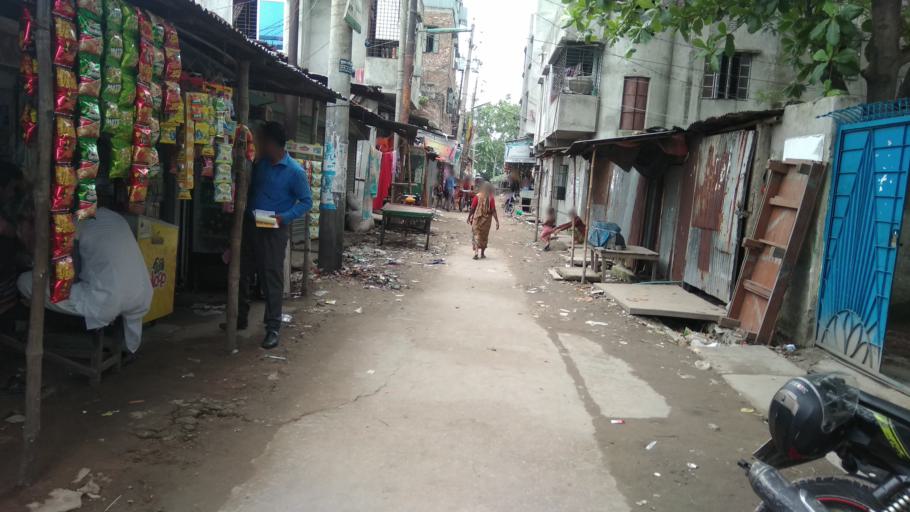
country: BD
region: Dhaka
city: Tungi
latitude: 23.8194
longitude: 90.3820
